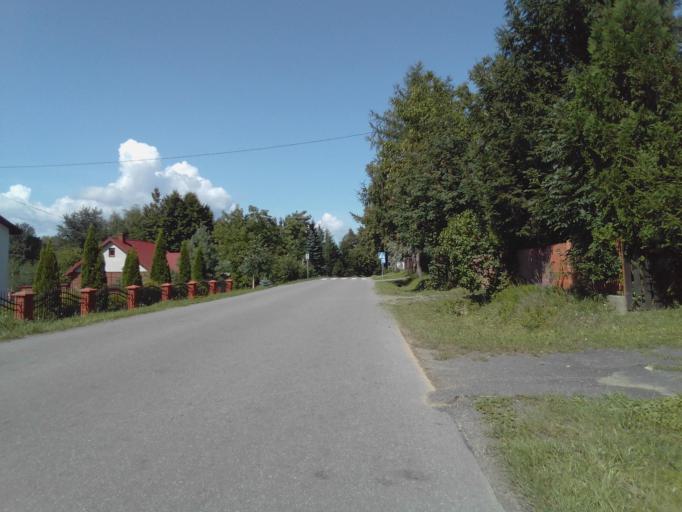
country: PL
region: Subcarpathian Voivodeship
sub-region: Powiat krosnienski
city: Chorkowka
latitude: 49.6124
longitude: 21.6039
